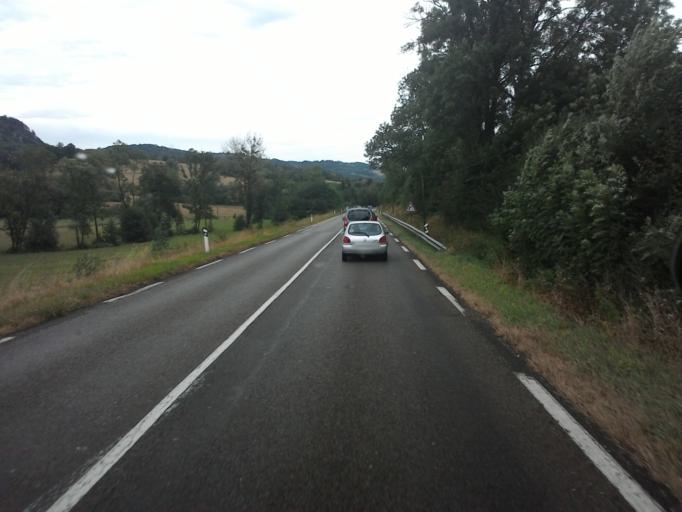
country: FR
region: Franche-Comte
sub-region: Departement du Jura
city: Poligny
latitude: 46.8534
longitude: 5.7115
